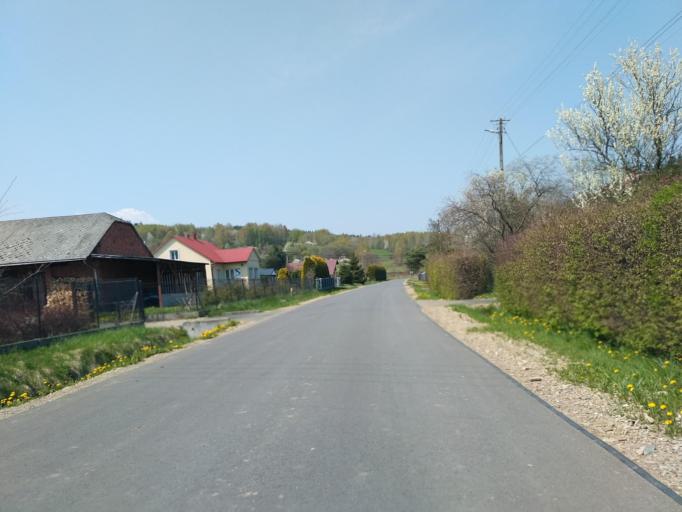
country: PL
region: Subcarpathian Voivodeship
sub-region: Powiat krosnienski
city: Chorkowka
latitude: 49.6346
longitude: 21.6920
